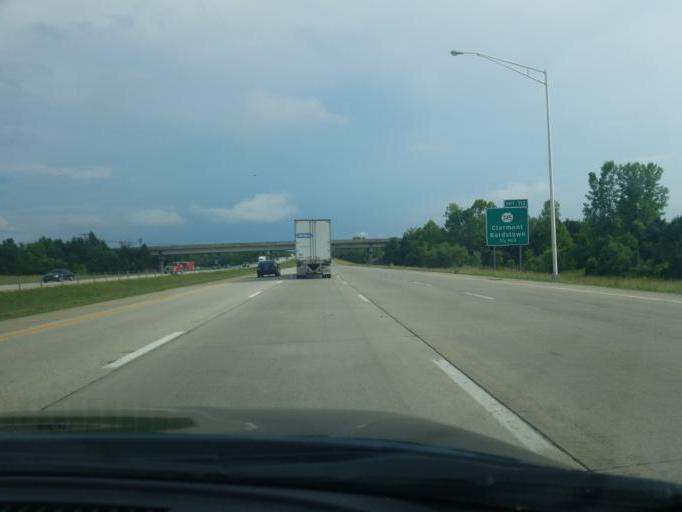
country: US
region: Kentucky
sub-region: Bullitt County
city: Shepherdsville
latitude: 37.9404
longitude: -85.6888
